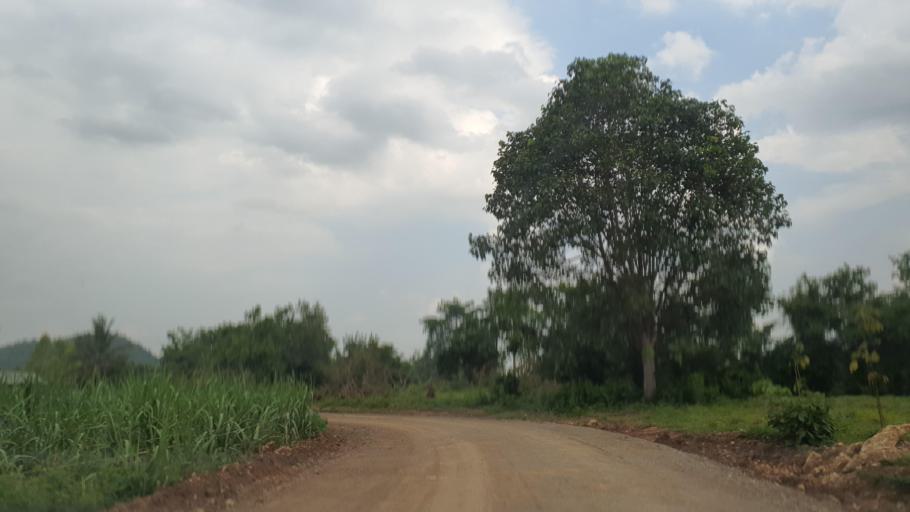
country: TH
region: Sukhothai
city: Thung Saliam
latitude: 17.2516
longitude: 99.5427
